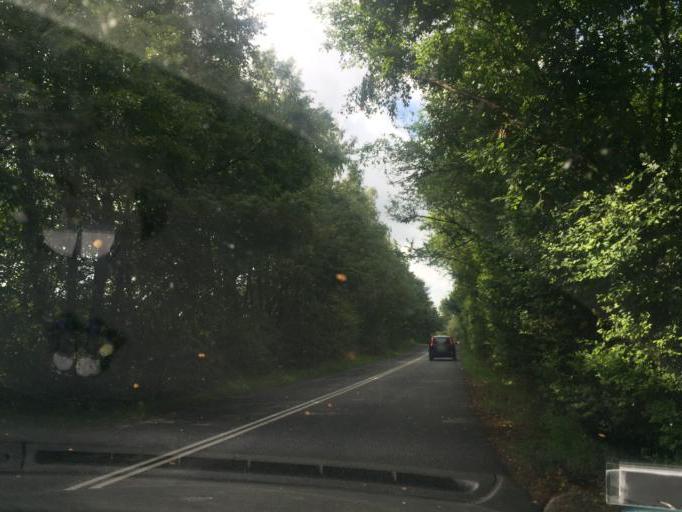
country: DK
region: Capital Region
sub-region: Allerod Kommune
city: Blovstrod
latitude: 55.8456
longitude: 12.3889
